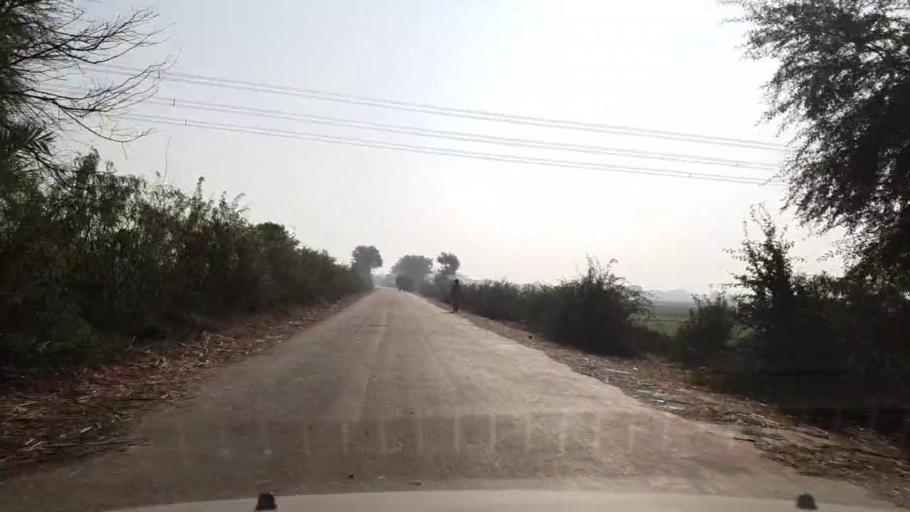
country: PK
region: Sindh
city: Matiari
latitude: 25.5746
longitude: 68.5069
